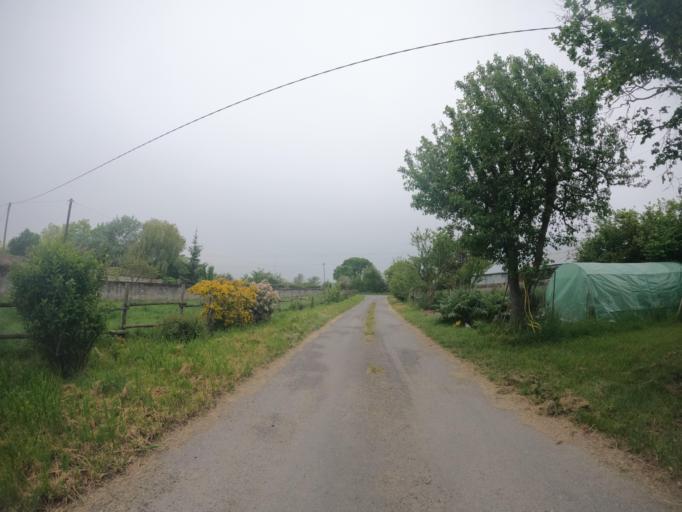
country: FR
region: Poitou-Charentes
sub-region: Departement des Deux-Sevres
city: Mauze-Thouarsais
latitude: 46.9030
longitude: -0.3394
